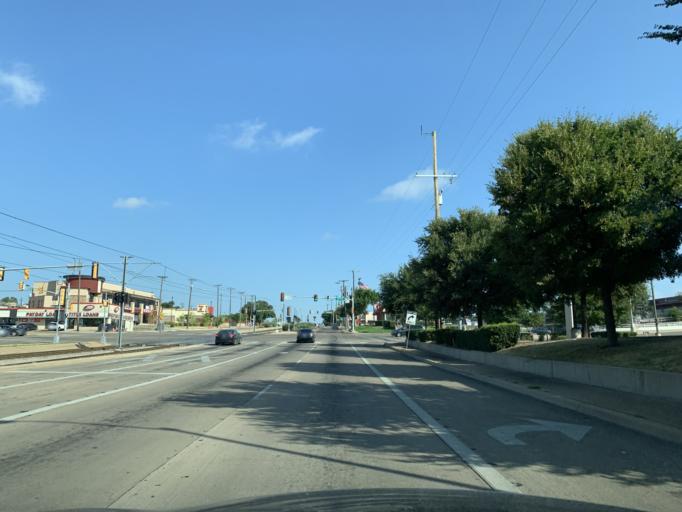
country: US
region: Texas
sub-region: Dallas County
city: Dallas
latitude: 32.7080
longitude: -96.8015
